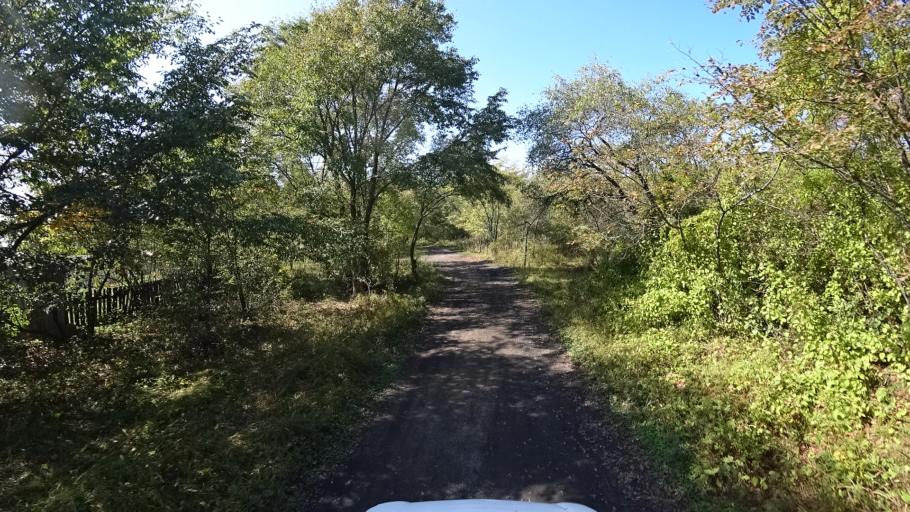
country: RU
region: Amur
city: Arkhara
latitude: 49.4008
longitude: 130.1273
